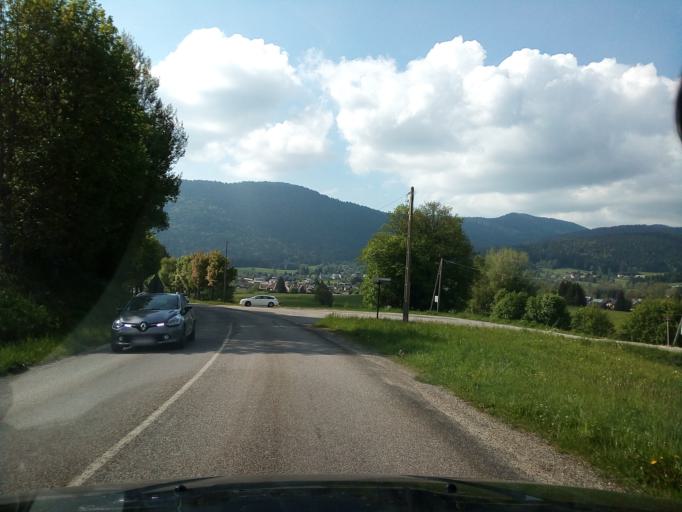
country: FR
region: Rhone-Alpes
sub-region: Departement de l'Isere
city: Autrans
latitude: 45.1704
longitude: 5.5519
